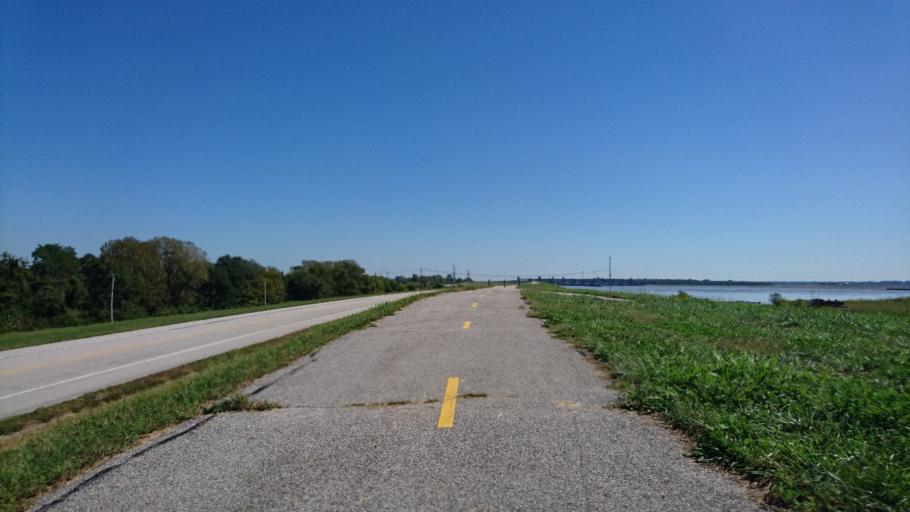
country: US
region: Illinois
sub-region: Madison County
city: Alton
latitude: 38.8846
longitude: -90.1711
